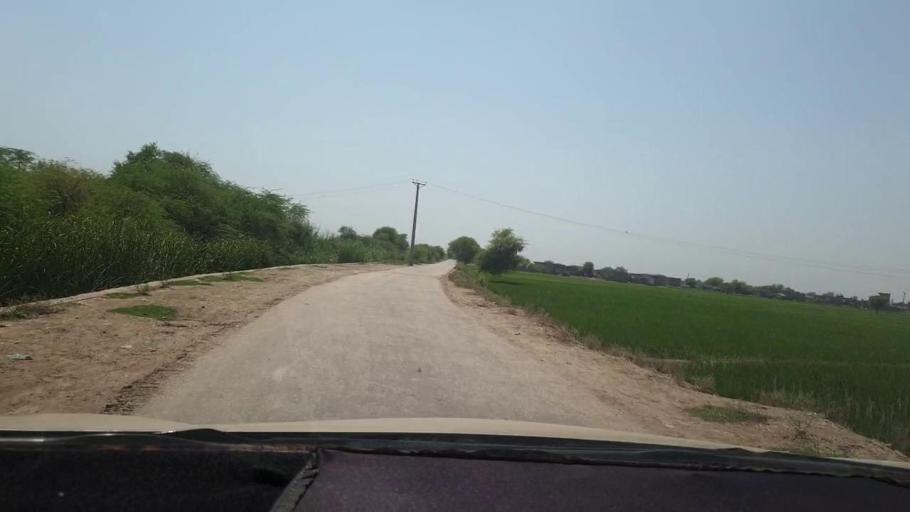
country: PK
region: Sindh
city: Shahdadkot
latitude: 27.8346
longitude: 67.9382
